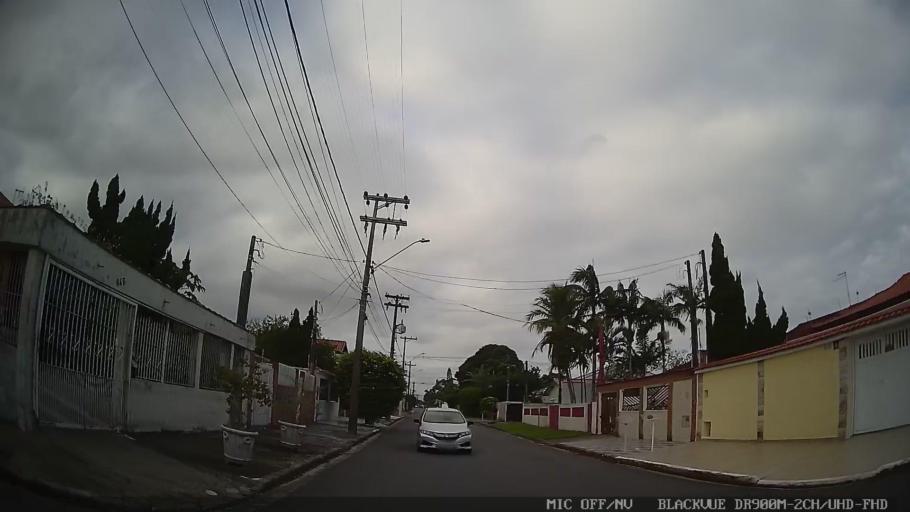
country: BR
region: Sao Paulo
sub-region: Peruibe
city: Peruibe
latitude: -24.3115
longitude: -46.9931
